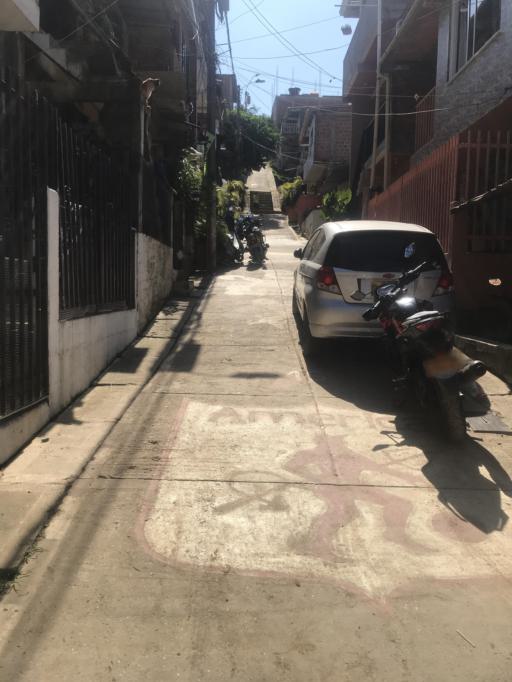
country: CO
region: Valle del Cauca
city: Cali
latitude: 3.3778
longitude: -76.5595
